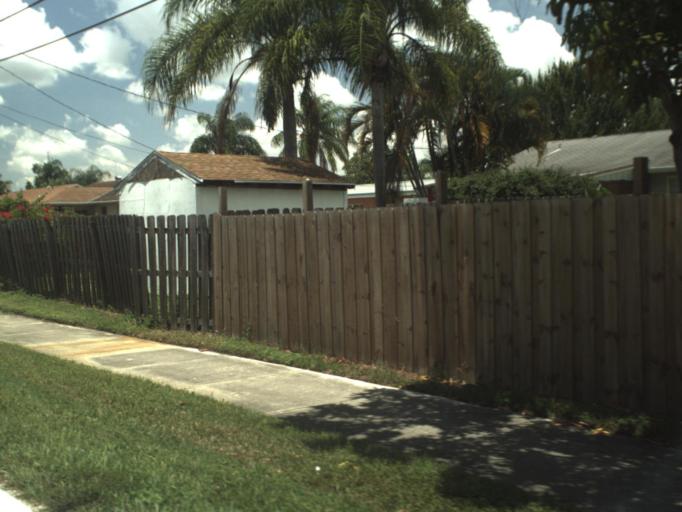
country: US
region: Florida
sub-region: Martin County
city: Port Salerno
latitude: 27.1320
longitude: -80.2120
